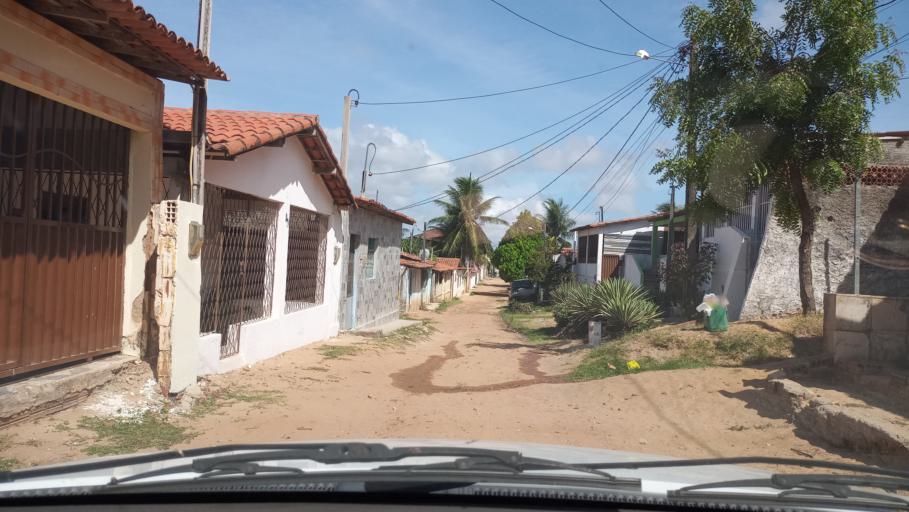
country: BR
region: Rio Grande do Norte
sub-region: Maxaranguape
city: Sao Miguel
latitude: -5.5154
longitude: -35.2637
